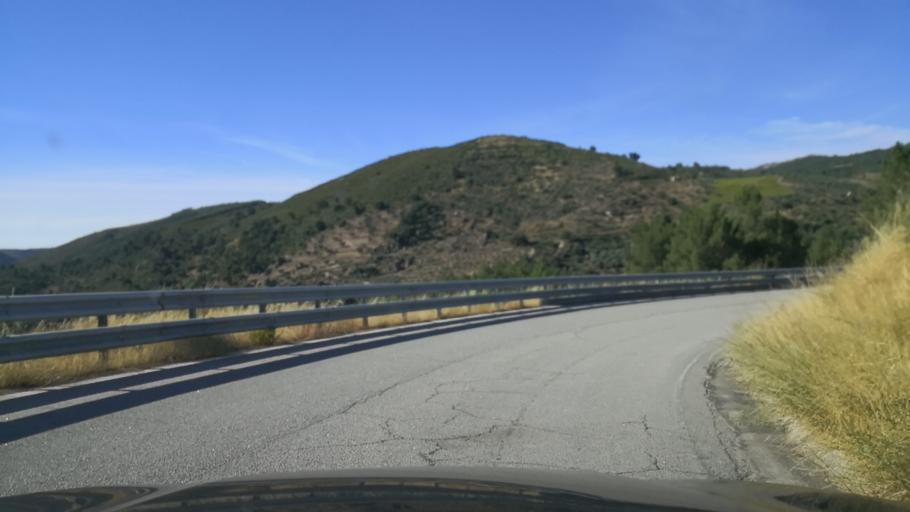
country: PT
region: Vila Real
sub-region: Murca
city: Murca
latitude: 41.4079
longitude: -7.4722
